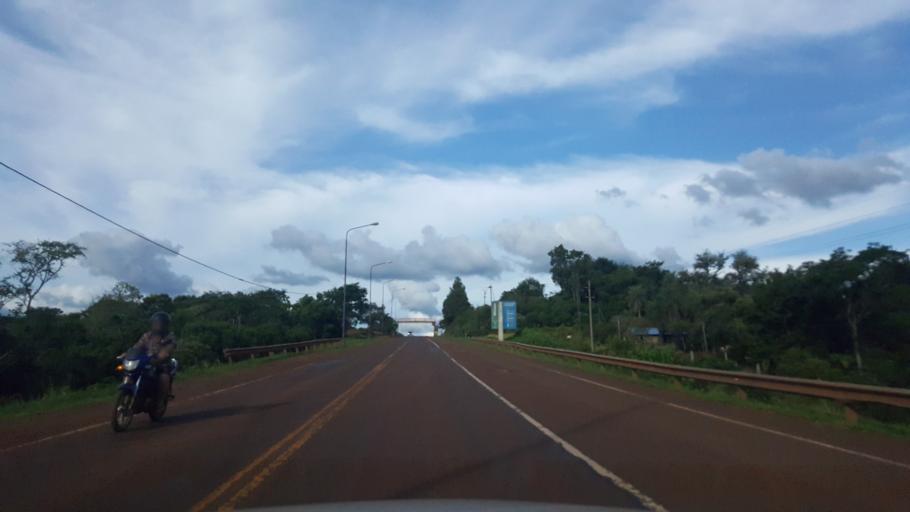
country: AR
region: Misiones
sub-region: Departamento de San Ignacio
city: San Ignacio
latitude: -27.2638
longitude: -55.5348
